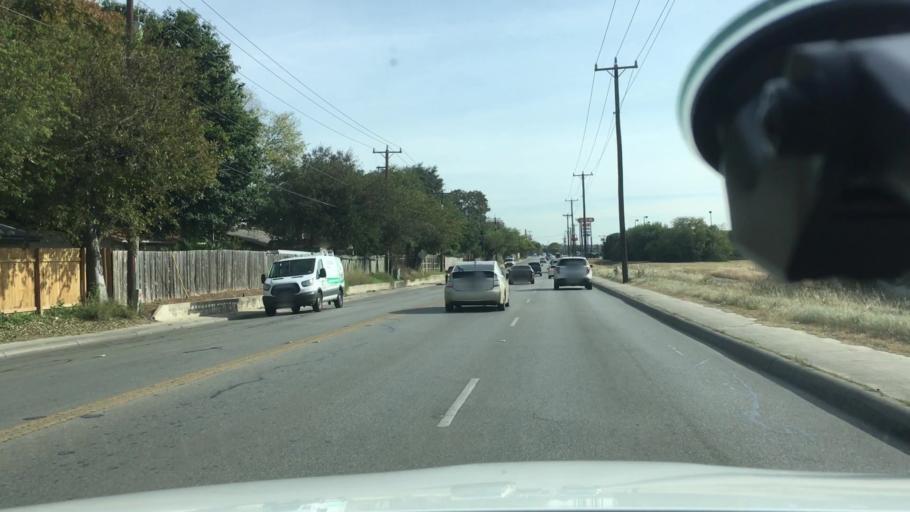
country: US
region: Texas
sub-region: Bexar County
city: Live Oak
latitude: 29.5731
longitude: -98.3879
